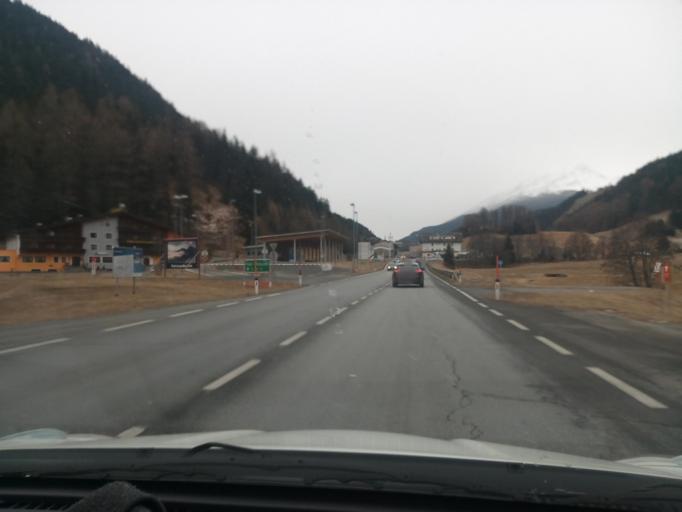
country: AT
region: Tyrol
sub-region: Politischer Bezirk Landeck
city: Nauders
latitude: 46.8503
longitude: 10.5048
